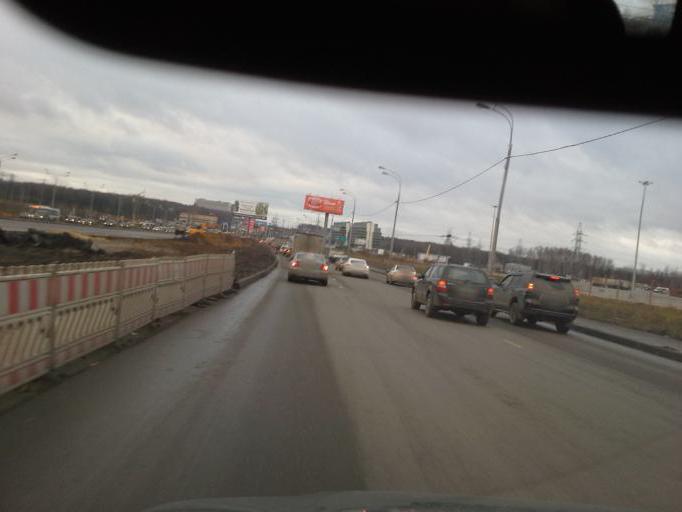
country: RU
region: Moscow
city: Tyoply Stan
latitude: 55.5992
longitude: 37.4814
